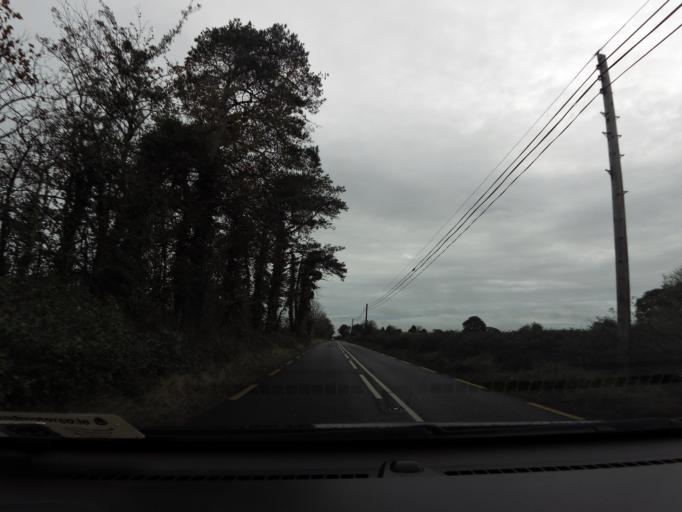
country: IE
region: Connaught
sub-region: County Galway
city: Tuam
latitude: 53.5995
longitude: -8.7638
